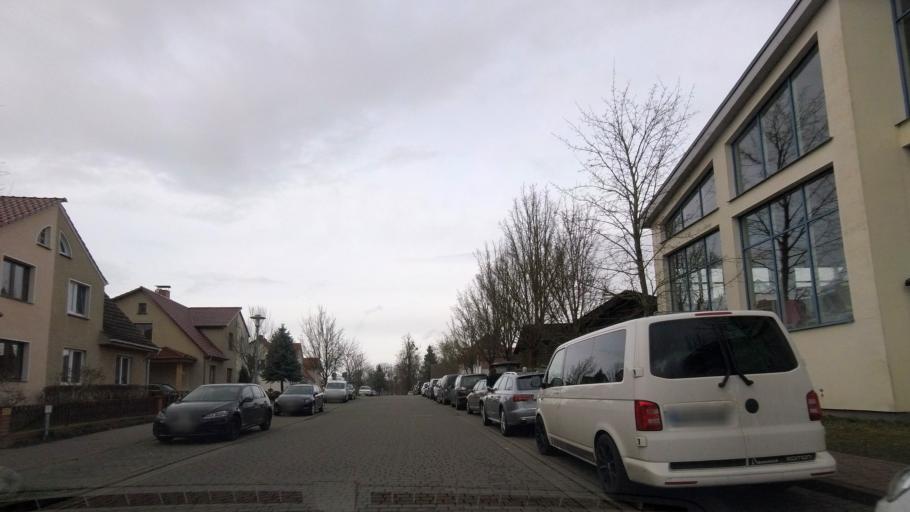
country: DE
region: Mecklenburg-Vorpommern
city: Robel
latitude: 53.3755
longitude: 12.6023
